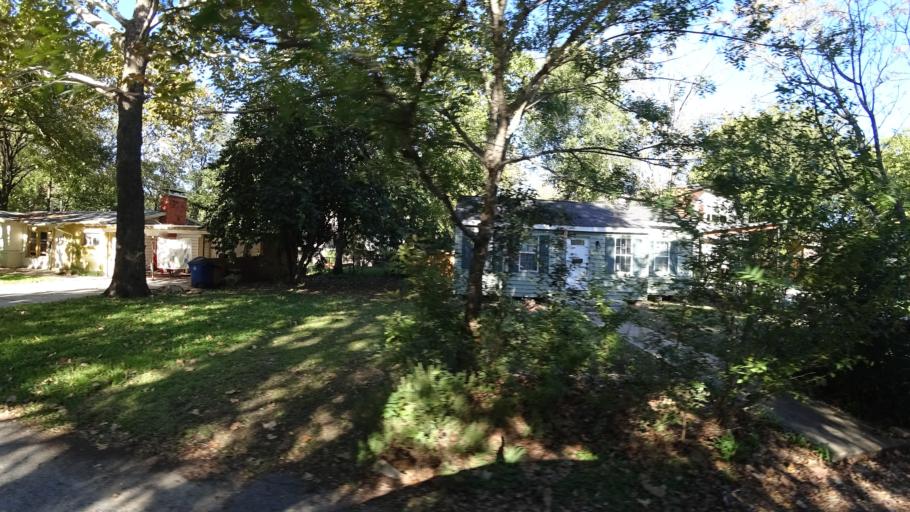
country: US
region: Texas
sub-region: Travis County
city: Austin
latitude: 30.3114
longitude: -97.7279
